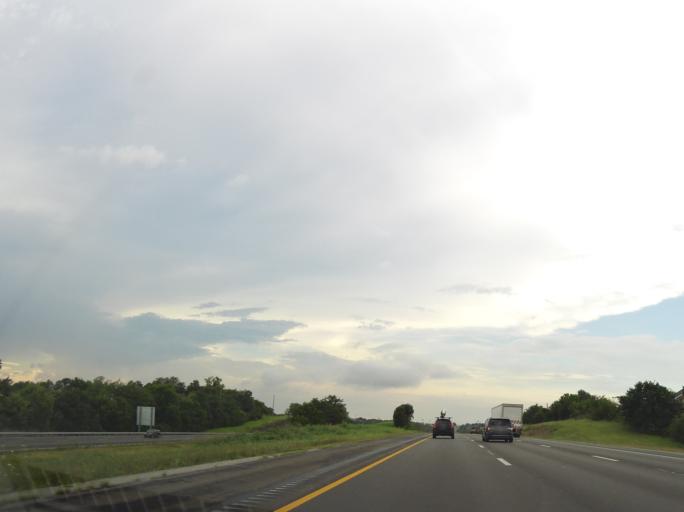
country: US
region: Kentucky
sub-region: Madison County
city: Richmond
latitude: 37.7129
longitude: -84.3201
